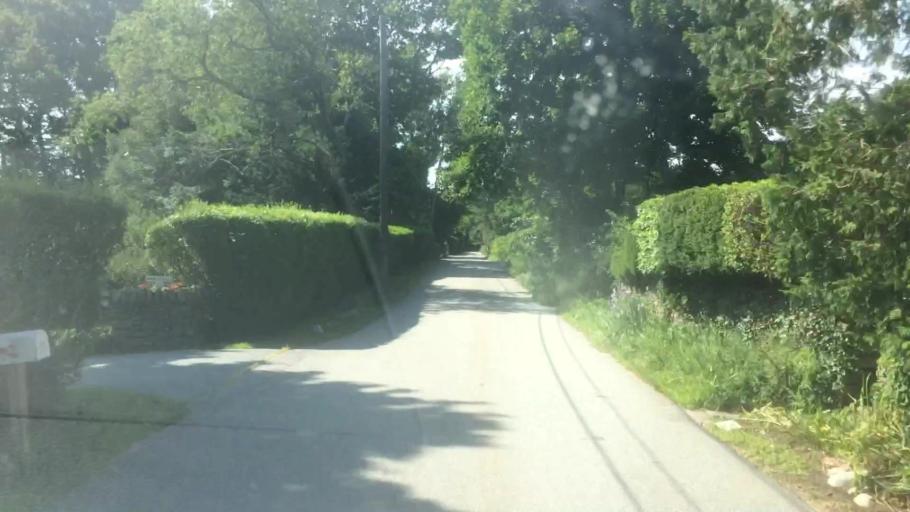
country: US
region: Rhode Island
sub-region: Newport County
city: Jamestown
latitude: 41.5078
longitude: -71.4193
